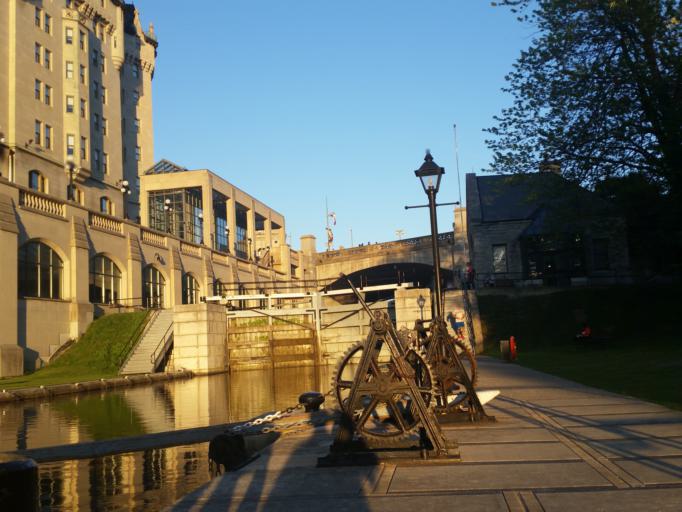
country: CA
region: Ontario
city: Ottawa
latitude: 45.4253
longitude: -75.6962
